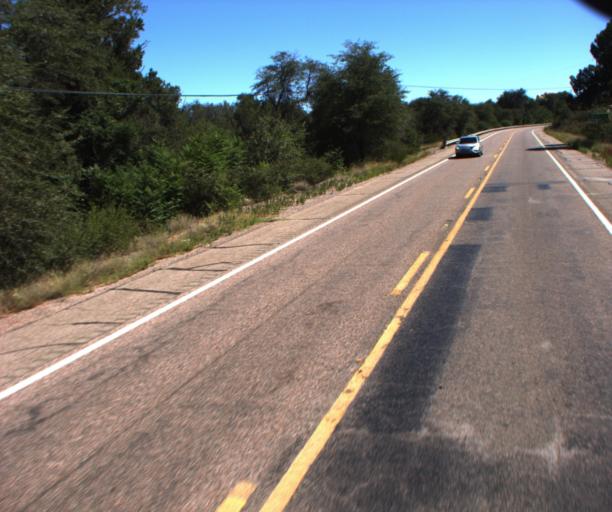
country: US
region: Arizona
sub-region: Pinal County
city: Superior
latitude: 33.3486
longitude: -110.9923
